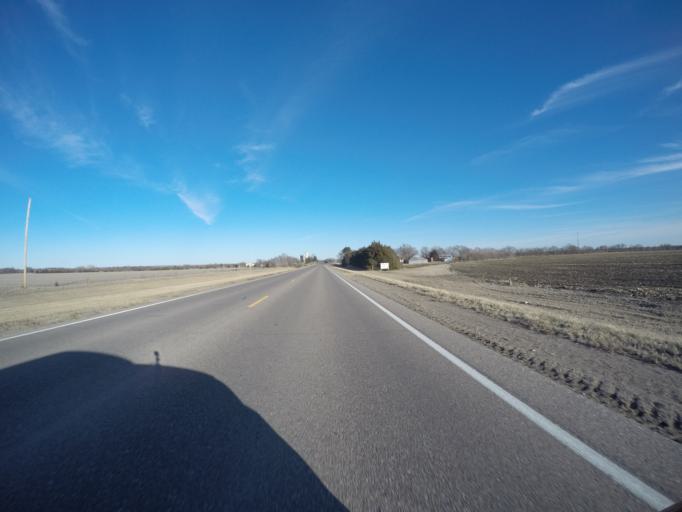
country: US
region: Nebraska
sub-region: Gage County
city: Wymore
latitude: 40.1395
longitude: -96.6844
